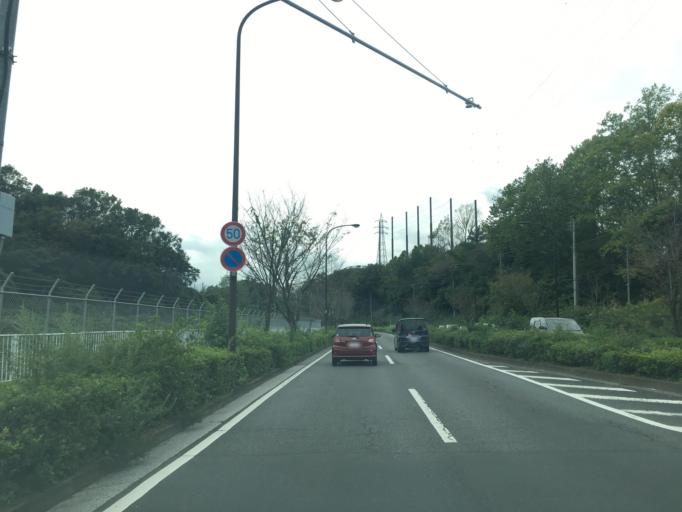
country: JP
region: Tokyo
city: Kokubunji
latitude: 35.6463
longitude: 139.4749
